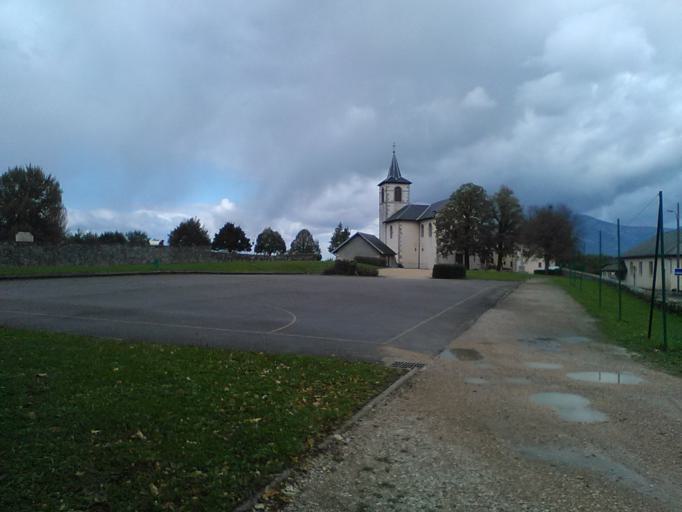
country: FR
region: Rhone-Alpes
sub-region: Departement de la Savoie
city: Jacob-Bellecombette
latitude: 45.5386
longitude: 5.9084
